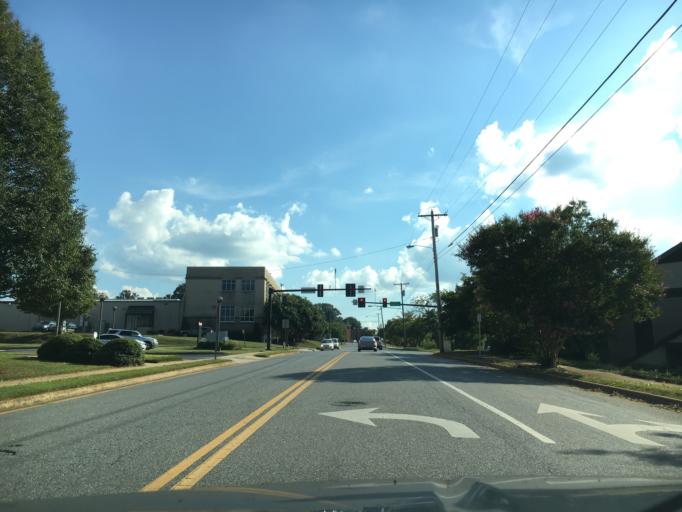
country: US
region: Virginia
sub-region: City of Lynchburg
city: West Lynchburg
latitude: 37.4140
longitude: -79.1697
